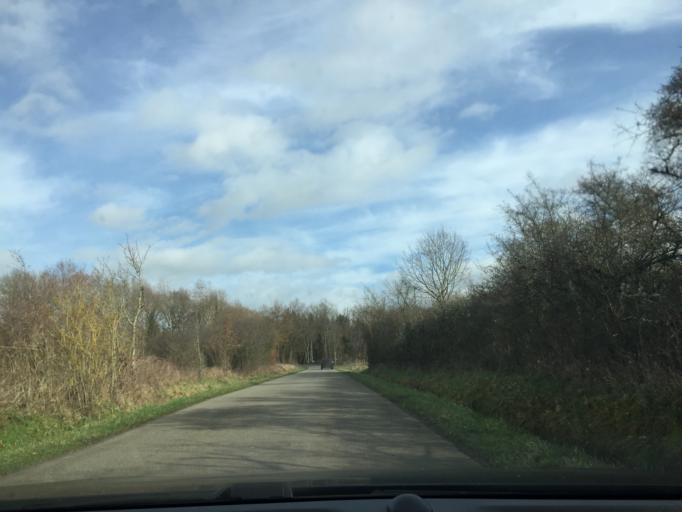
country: BE
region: Wallonia
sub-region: Province du Luxembourg
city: Hotton
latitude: 50.2915
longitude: 5.4855
